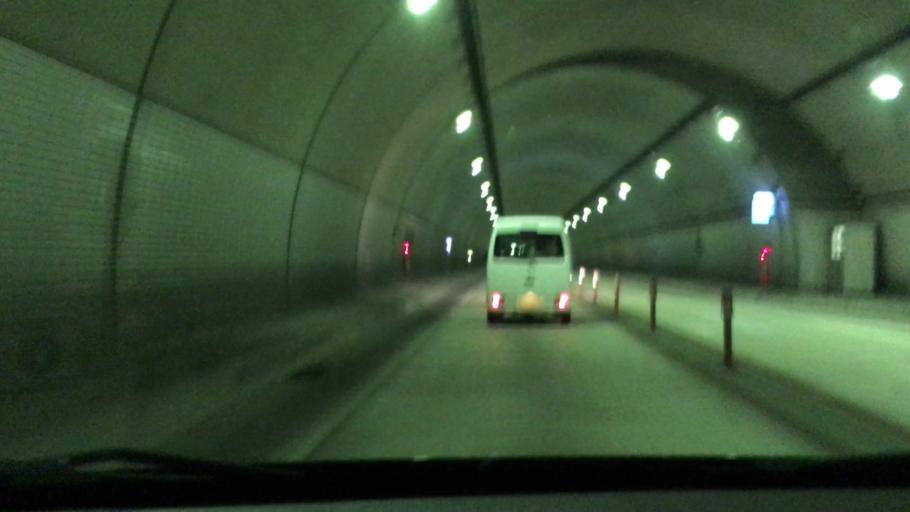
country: JP
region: Nagasaki
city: Sasebo
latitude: 33.0912
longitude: 129.7786
